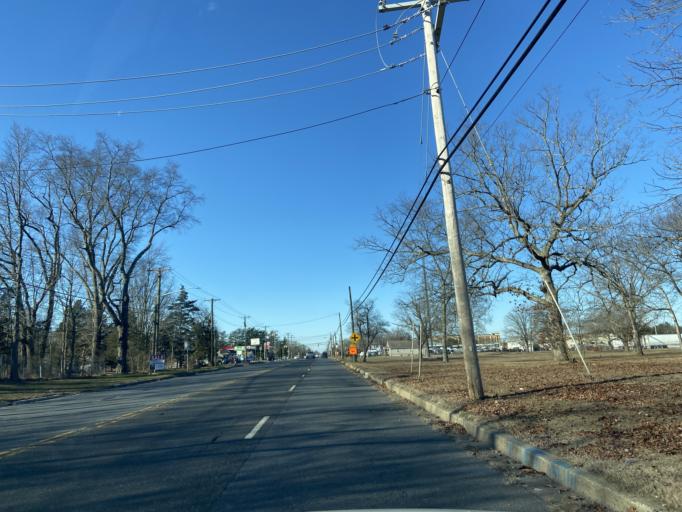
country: US
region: New Jersey
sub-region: Cumberland County
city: Vineland
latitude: 39.4878
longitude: -75.0588
